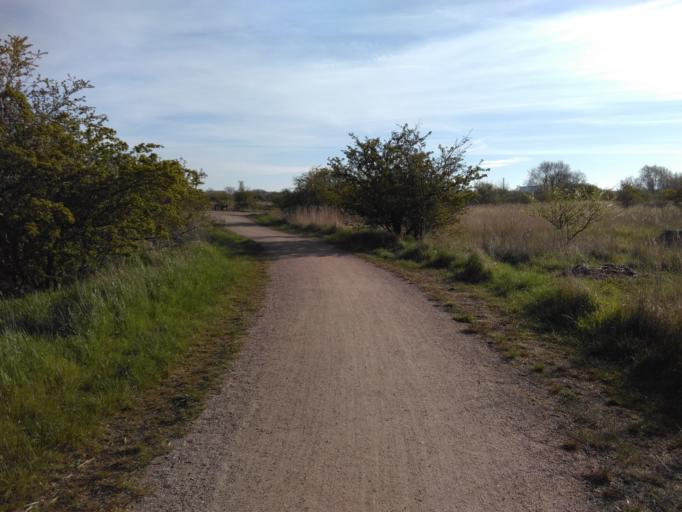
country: DK
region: Capital Region
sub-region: Kobenhavn
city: Copenhagen
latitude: 55.6500
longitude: 12.5716
